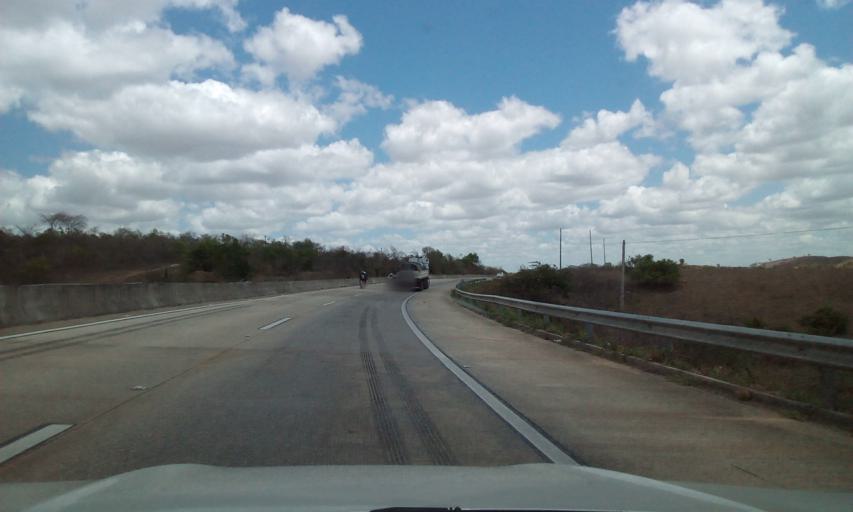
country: BR
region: Alagoas
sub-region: Porto Real Do Colegio
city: Porto Real do Colegio
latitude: -10.1543
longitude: -36.8114
